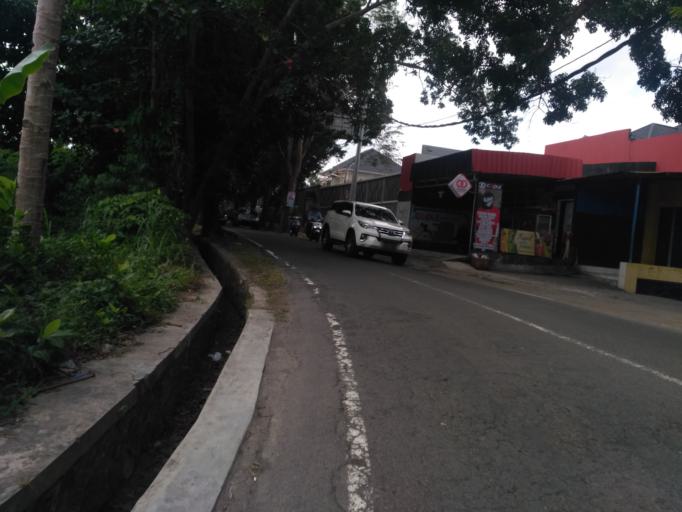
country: ID
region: Daerah Istimewa Yogyakarta
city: Melati
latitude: -7.7374
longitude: 110.3522
